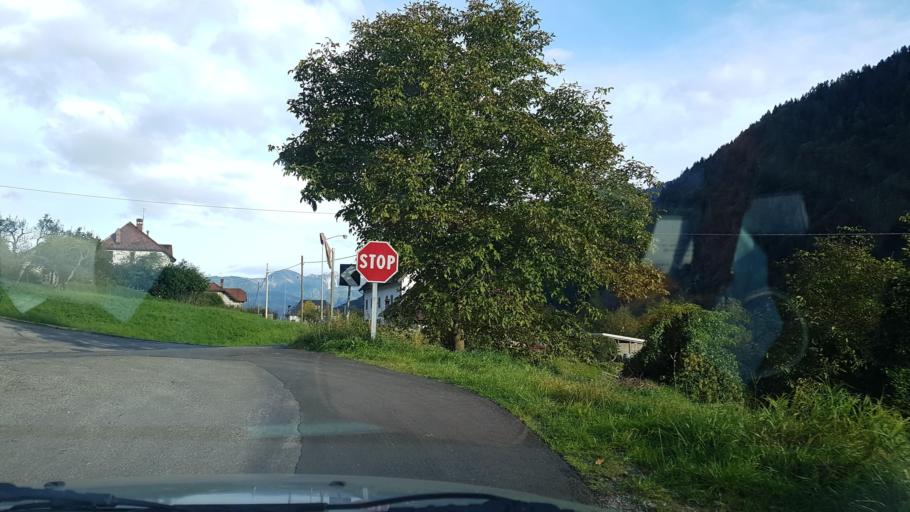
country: IT
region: Friuli Venezia Giulia
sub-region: Provincia di Udine
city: Pieria-Prato Carnico
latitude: 46.5218
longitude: 12.7768
